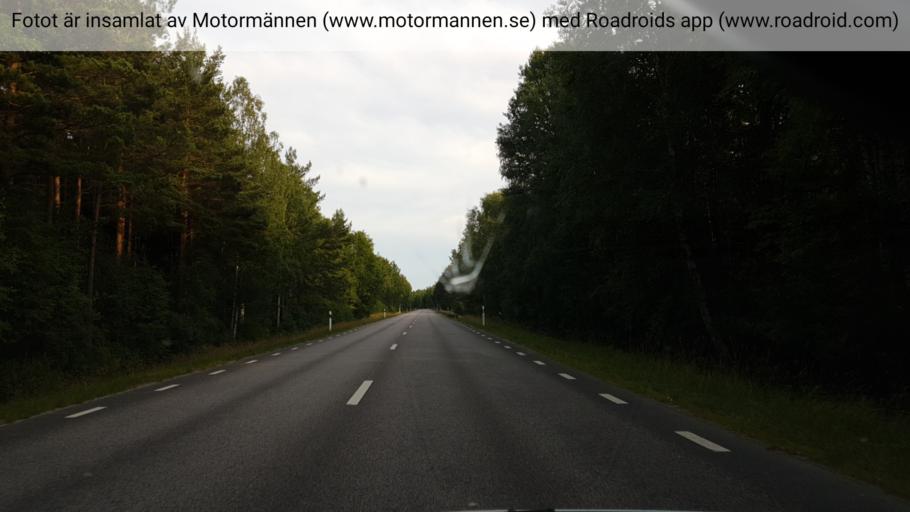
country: SE
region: Vaestra Goetaland
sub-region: Mariestads Kommun
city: Mariestad
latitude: 58.6752
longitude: 13.8513
